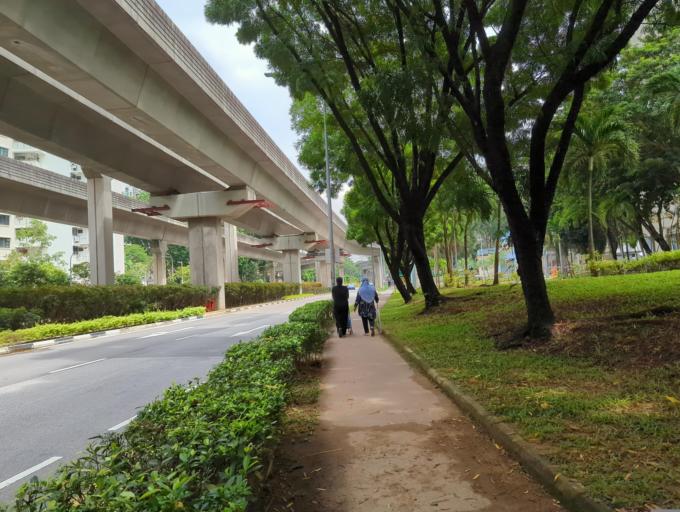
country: MY
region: Johor
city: Kampung Pasir Gudang Baru
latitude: 1.3958
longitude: 103.8952
